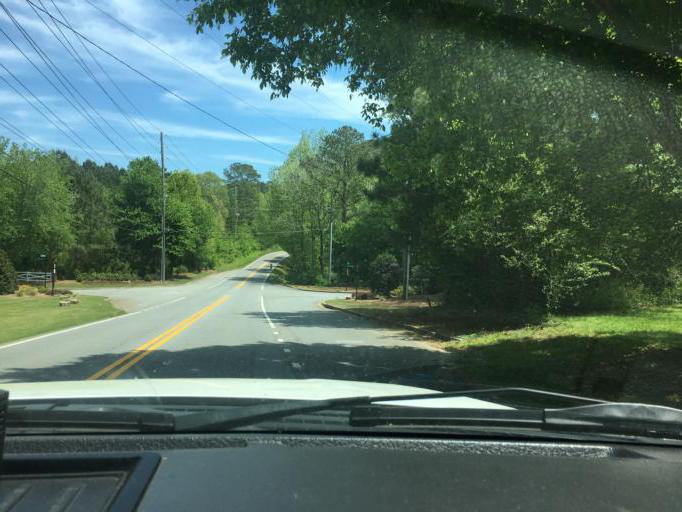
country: US
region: Georgia
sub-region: Fulton County
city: Milton
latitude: 34.1226
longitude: -84.3994
